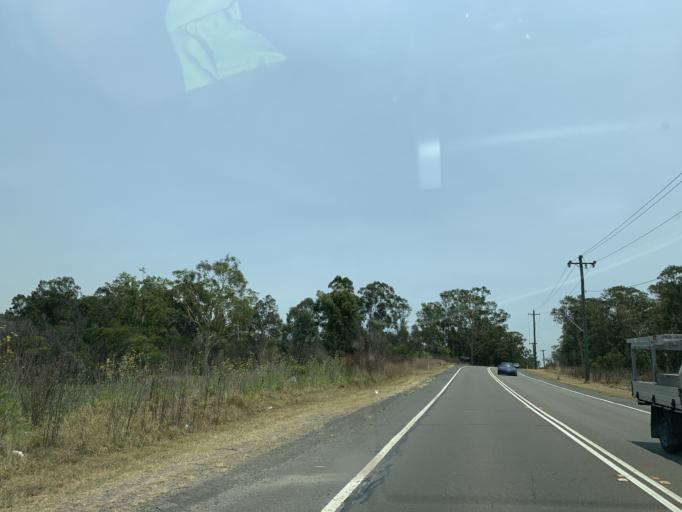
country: AU
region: New South Wales
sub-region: Fairfield
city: Horsley Park
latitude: -33.8308
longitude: 150.8735
